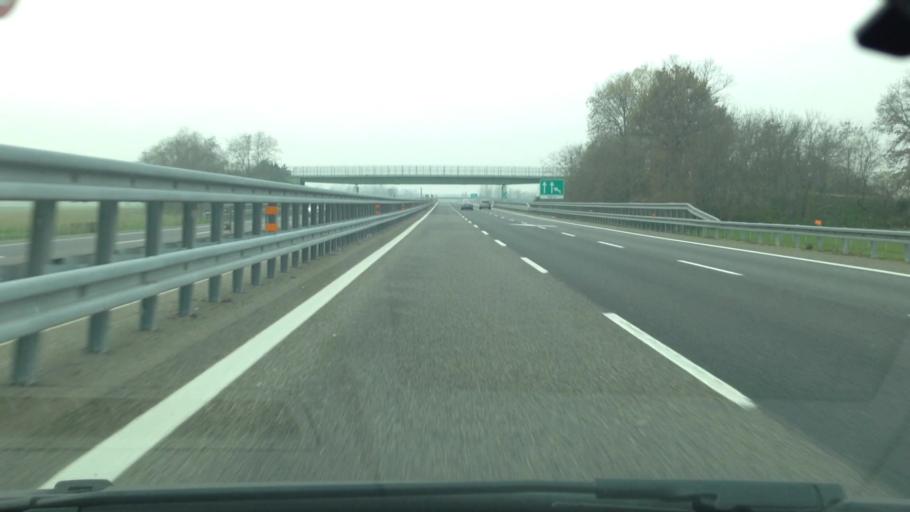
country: IT
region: Piedmont
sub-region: Provincia di Torino
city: Pessione
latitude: 44.9577
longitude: 7.8298
